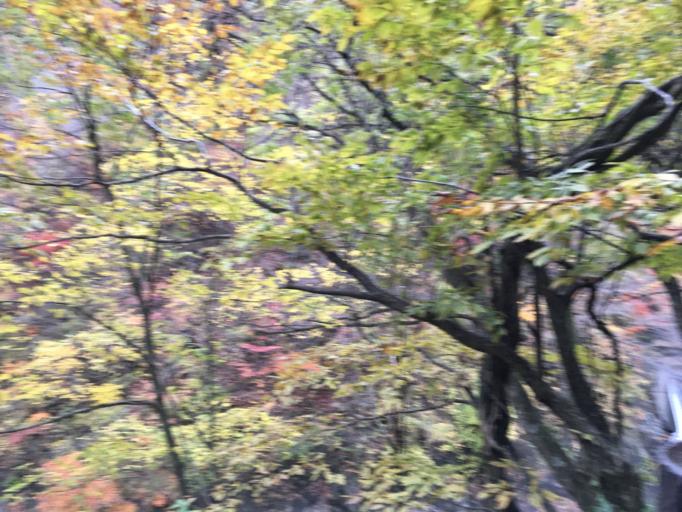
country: JP
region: Miyagi
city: Furukawa
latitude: 38.7293
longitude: 140.6904
